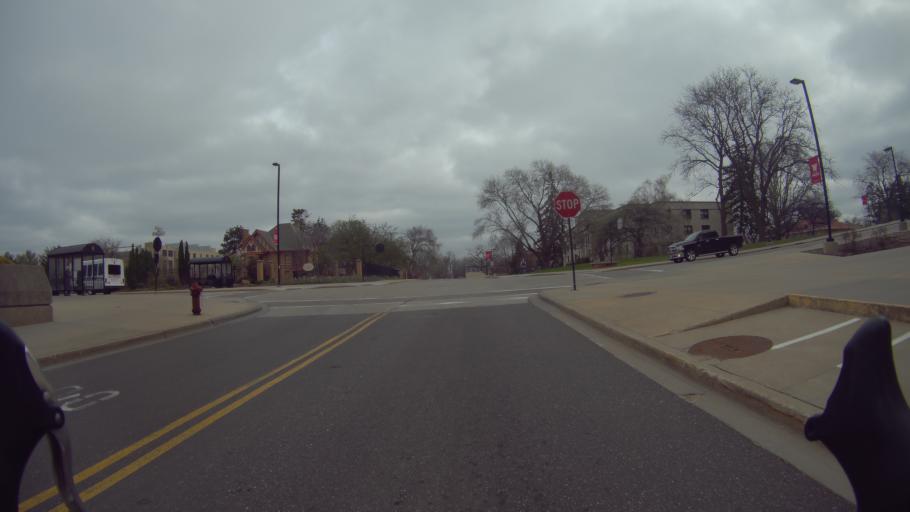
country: US
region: Wisconsin
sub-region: Dane County
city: Madison
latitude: 43.0761
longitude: -89.4127
